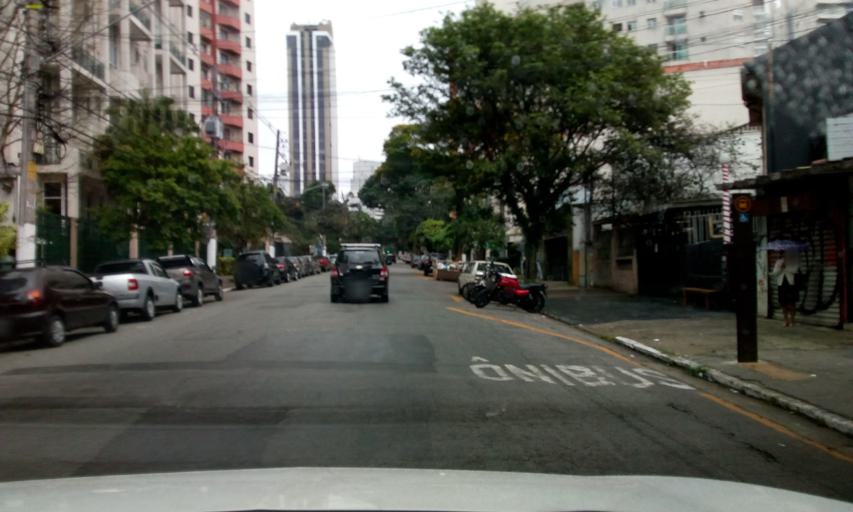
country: BR
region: Sao Paulo
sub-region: Sao Paulo
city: Sao Paulo
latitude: -23.5877
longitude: -46.6318
